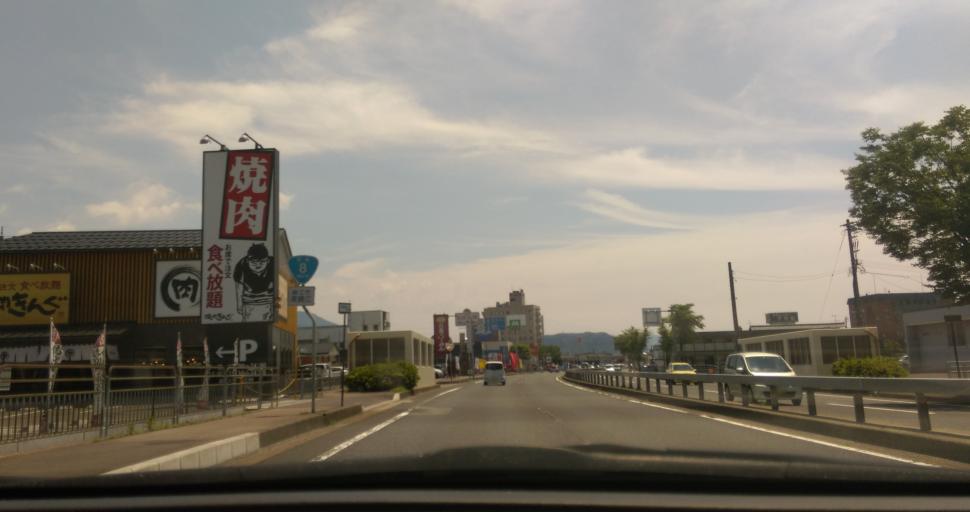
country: JP
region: Fukui
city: Sabae
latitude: 35.9455
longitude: 136.1945
